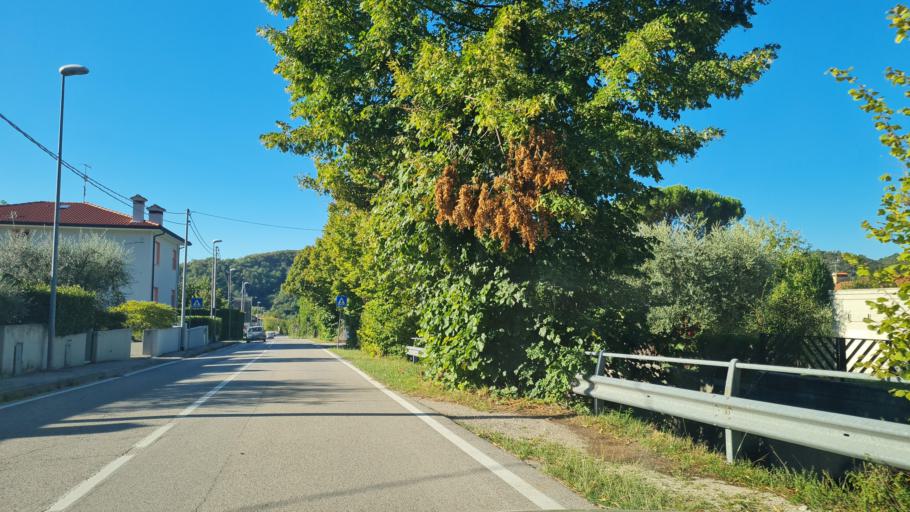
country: IT
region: Veneto
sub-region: Provincia di Vicenza
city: Campese
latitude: 45.7778
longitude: 11.6918
